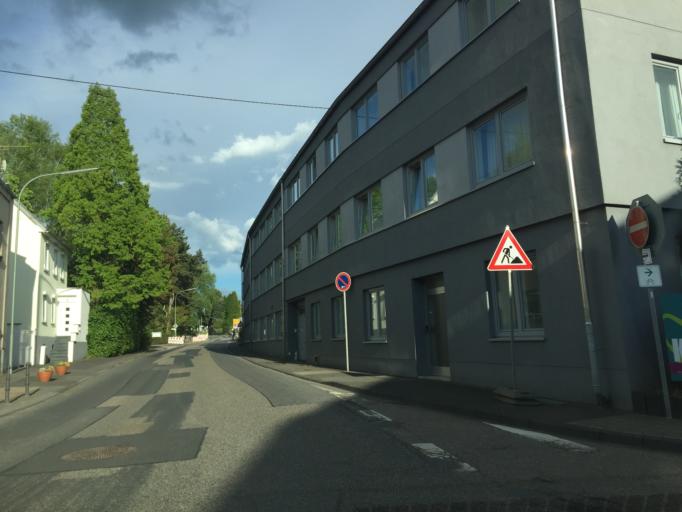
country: DE
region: Rheinland-Pfalz
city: Hohr-Grenzhausen
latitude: 50.4426
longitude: 7.6586
